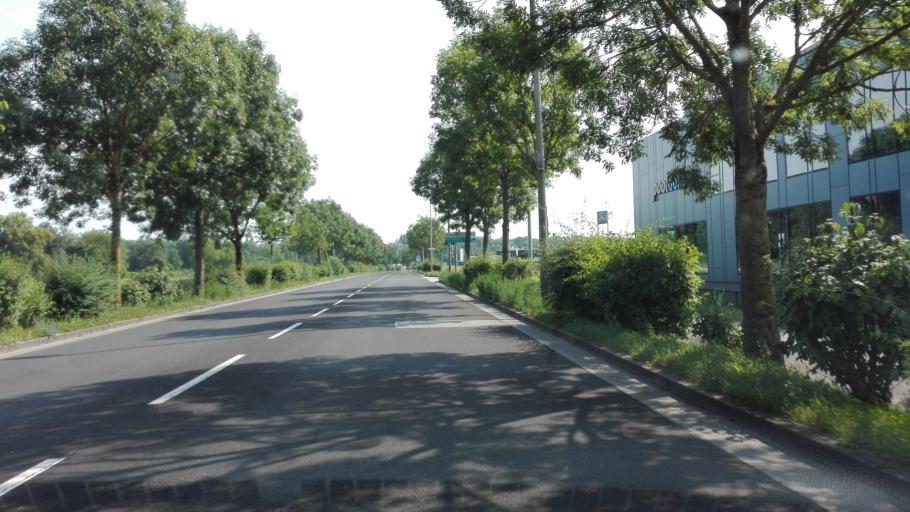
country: AT
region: Upper Austria
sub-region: Politischer Bezirk Linz-Land
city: Ansfelden
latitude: 48.2409
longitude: 14.2853
